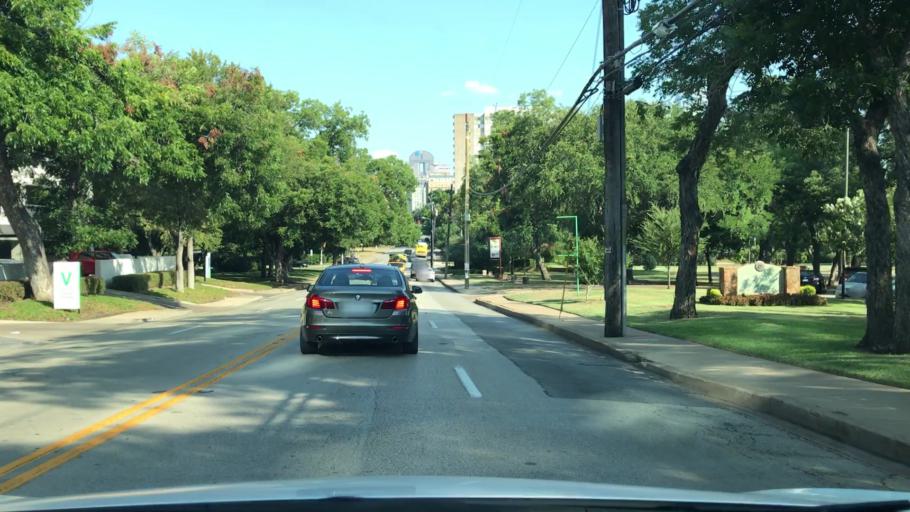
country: US
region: Texas
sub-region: Dallas County
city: Dallas
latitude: 32.8024
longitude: -96.8123
